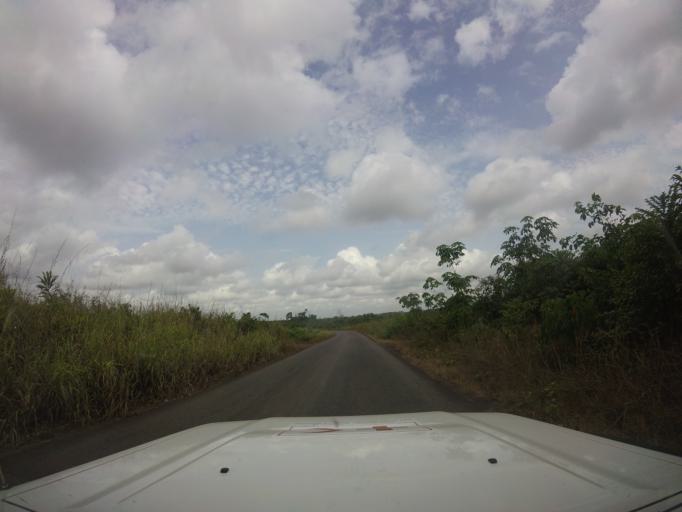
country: LR
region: Bomi
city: Tubmanburg
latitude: 6.7125
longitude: -10.9374
